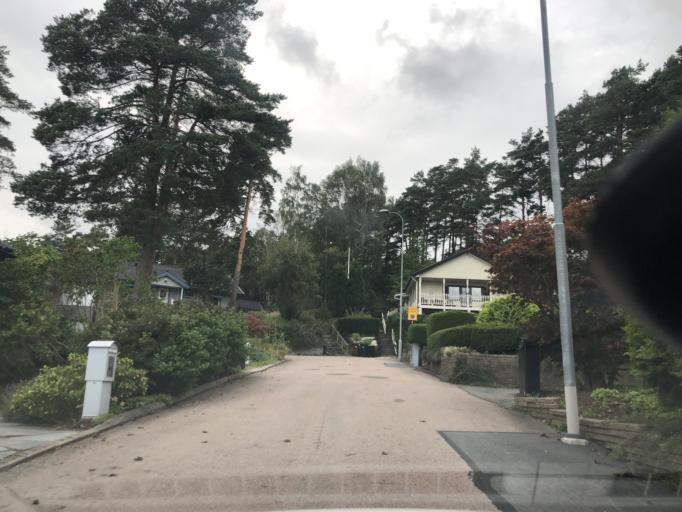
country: SE
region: Vaestra Goetaland
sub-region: Goteborg
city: Goeteborg
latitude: 57.7567
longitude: 11.9593
